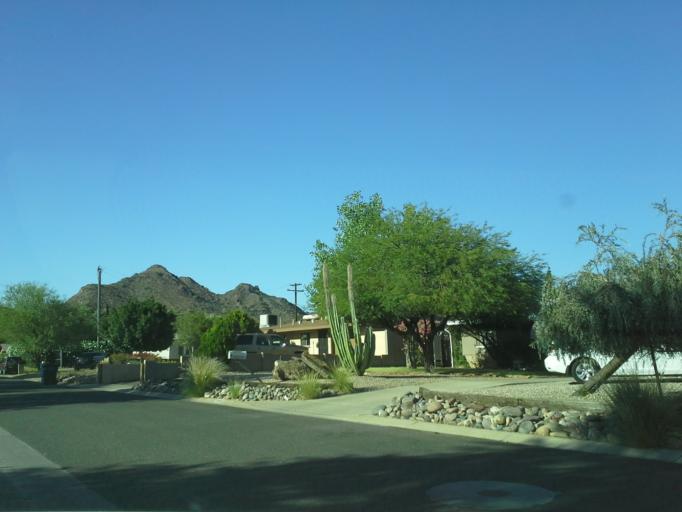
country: US
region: Arizona
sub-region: Maricopa County
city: Phoenix
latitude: 33.5551
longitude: -112.0523
